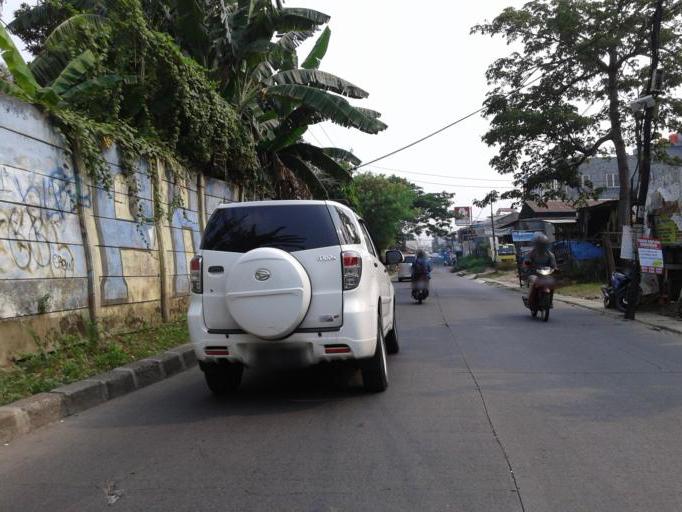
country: ID
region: West Java
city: Sawangan
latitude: -6.3630
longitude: 106.7760
